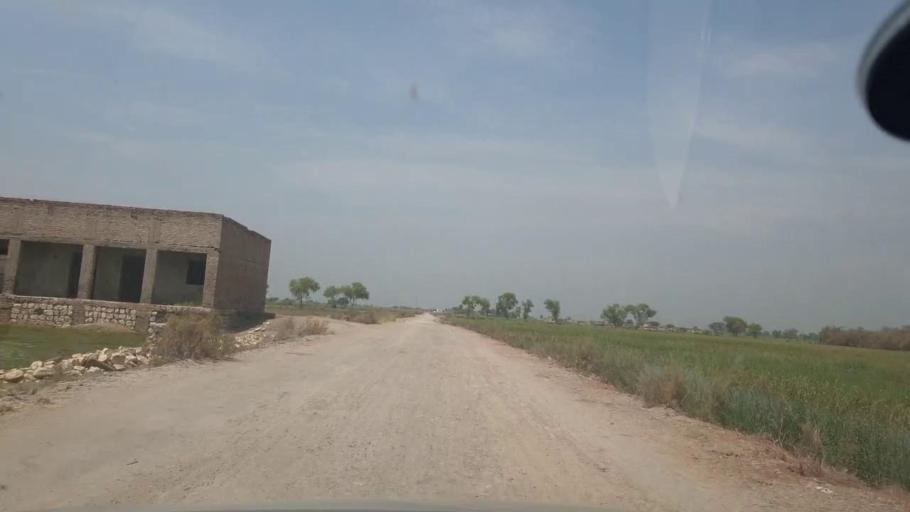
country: PK
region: Sindh
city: Thul
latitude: 28.1690
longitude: 68.6344
